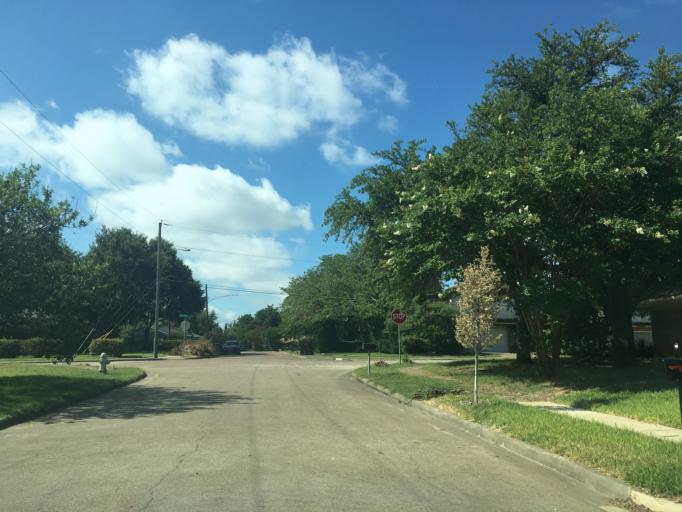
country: US
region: Texas
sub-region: Dallas County
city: Garland
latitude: 32.8477
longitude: -96.6647
